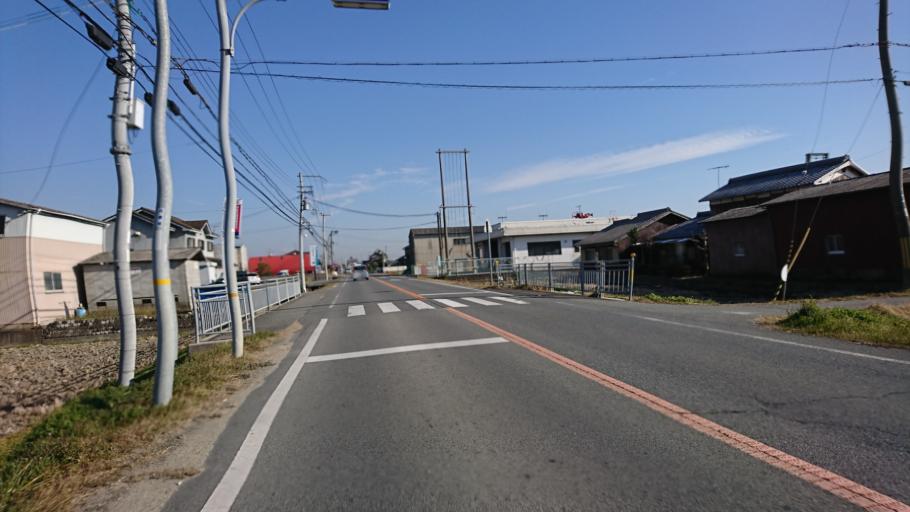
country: JP
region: Hyogo
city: Kakogawacho-honmachi
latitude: 34.7995
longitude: 134.8865
